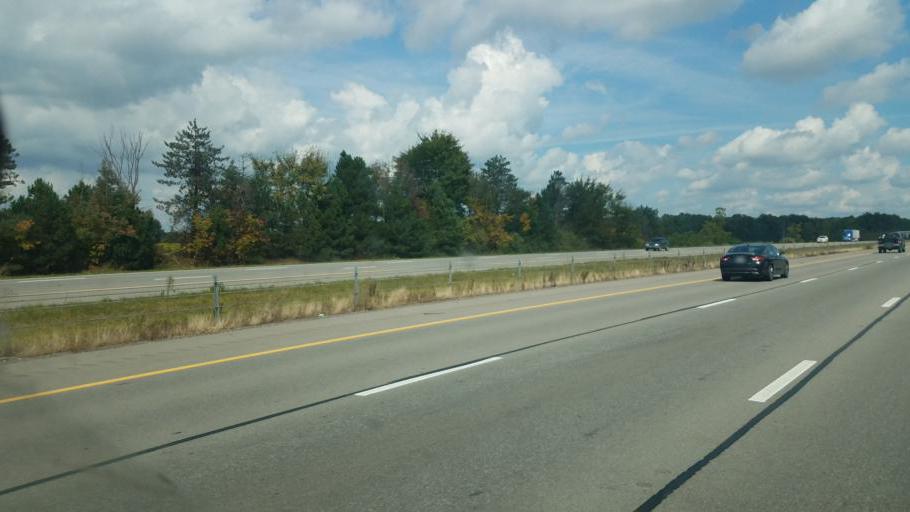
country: US
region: Ohio
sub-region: Morrow County
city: Mount Gilead
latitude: 40.4490
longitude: -82.7911
